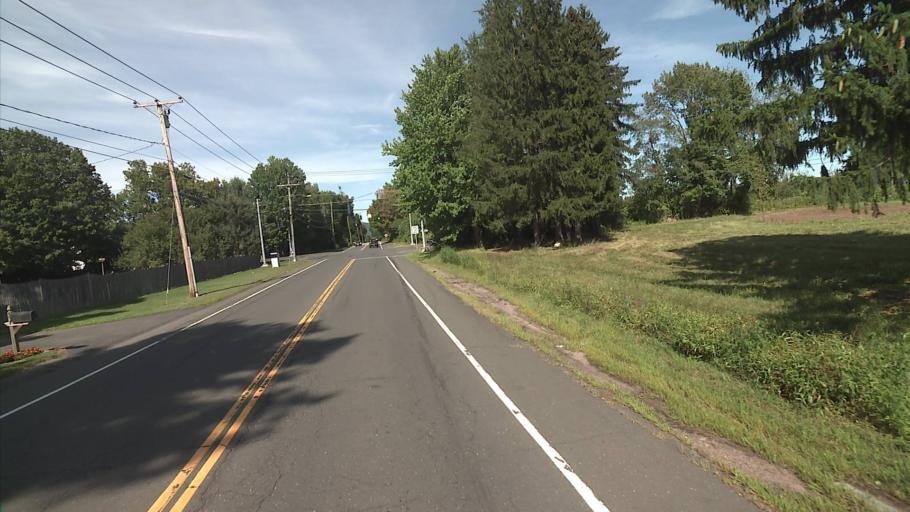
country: US
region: Connecticut
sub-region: New Haven County
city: Cheshire Village
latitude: 41.5116
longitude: -72.8747
